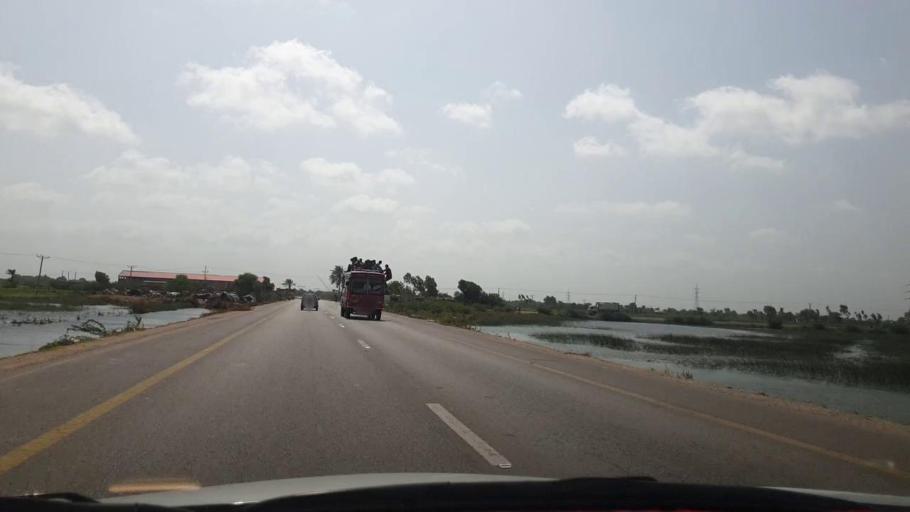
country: PK
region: Sindh
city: Talhar
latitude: 24.9145
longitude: 68.7290
